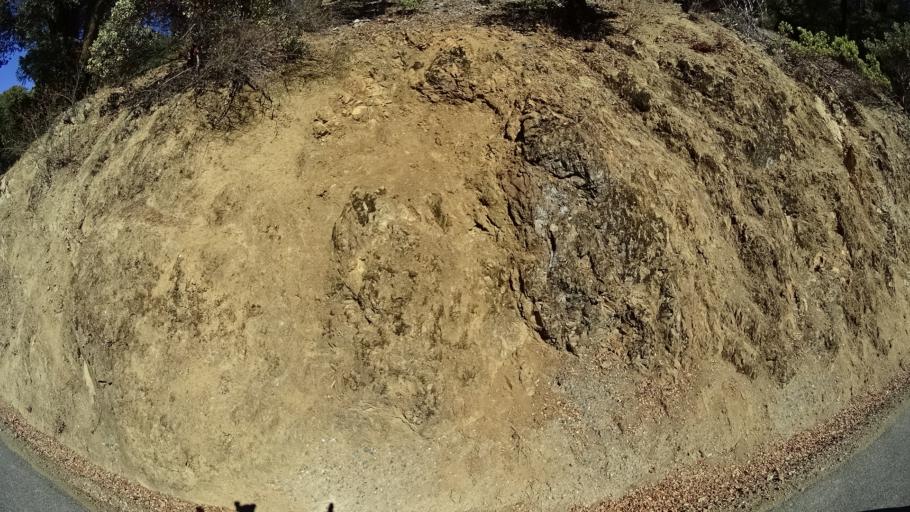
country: US
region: California
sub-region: Siskiyou County
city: Happy Camp
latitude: 41.3051
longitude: -123.1635
